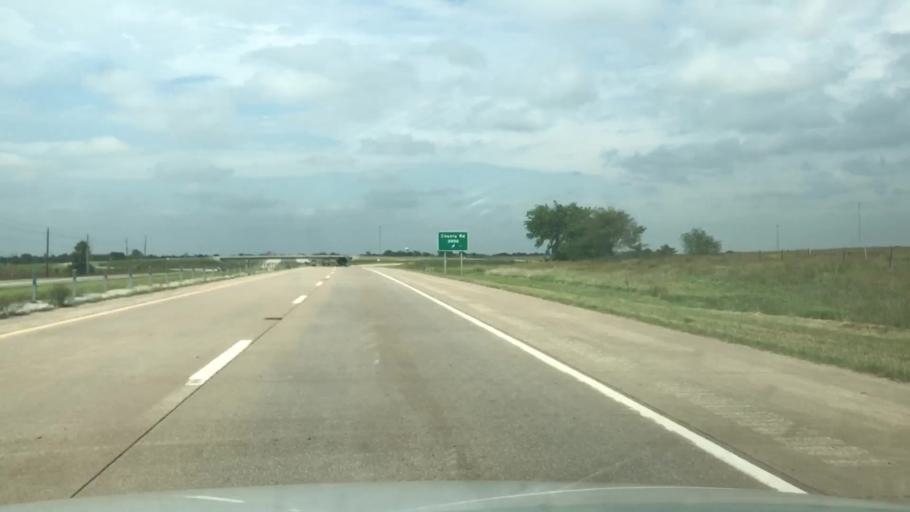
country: US
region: Oklahoma
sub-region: Washington County
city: Bartlesville
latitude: 36.5779
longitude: -95.9294
